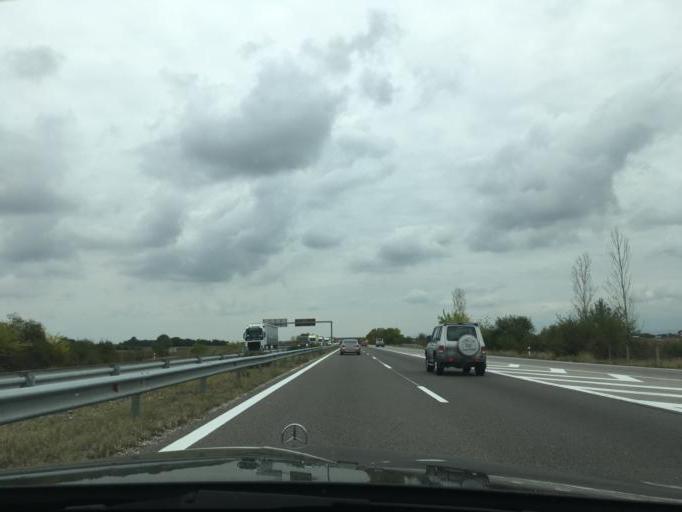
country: BG
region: Pazardzhik
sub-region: Obshtina Pazardzhik
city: Pazardzhik
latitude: 42.2603
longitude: 24.3194
